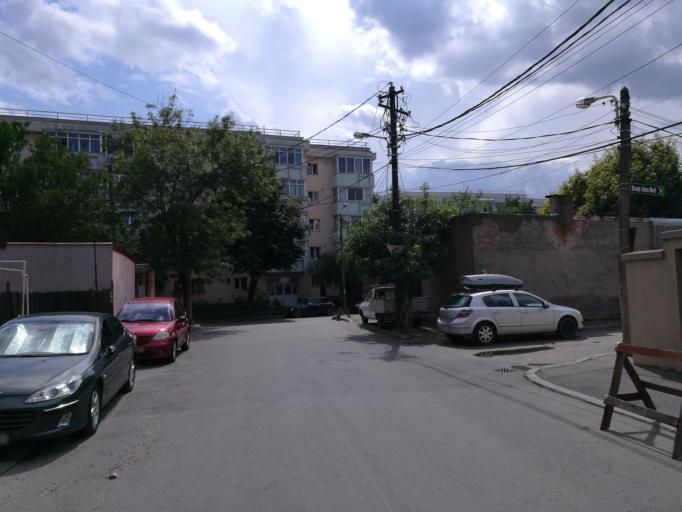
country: RO
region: Bucuresti
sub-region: Municipiul Bucuresti
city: Bucharest
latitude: 44.4853
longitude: 26.1012
